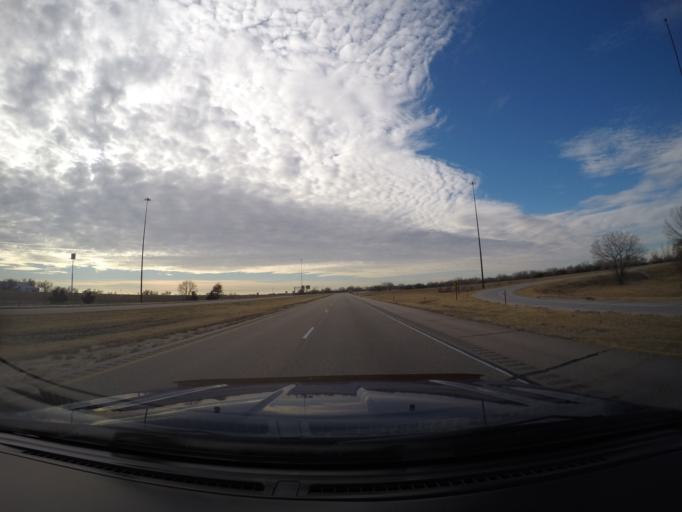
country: US
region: Nebraska
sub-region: Hall County
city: Grand Island
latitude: 40.8202
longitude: -98.3792
